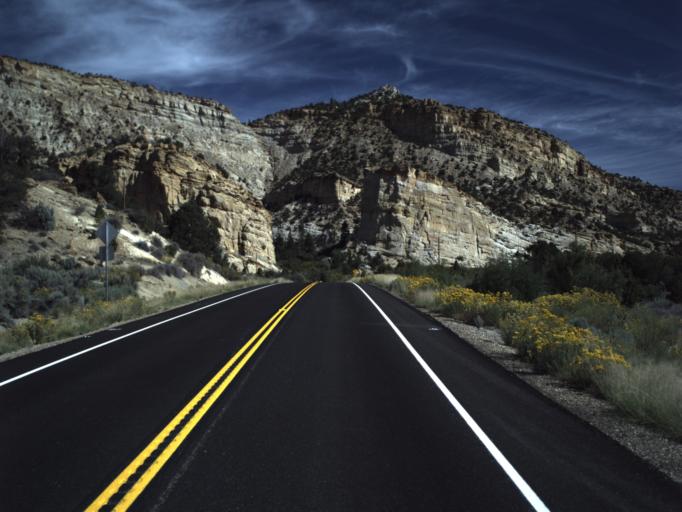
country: US
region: Utah
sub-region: Garfield County
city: Panguitch
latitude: 37.5993
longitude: -111.9185
